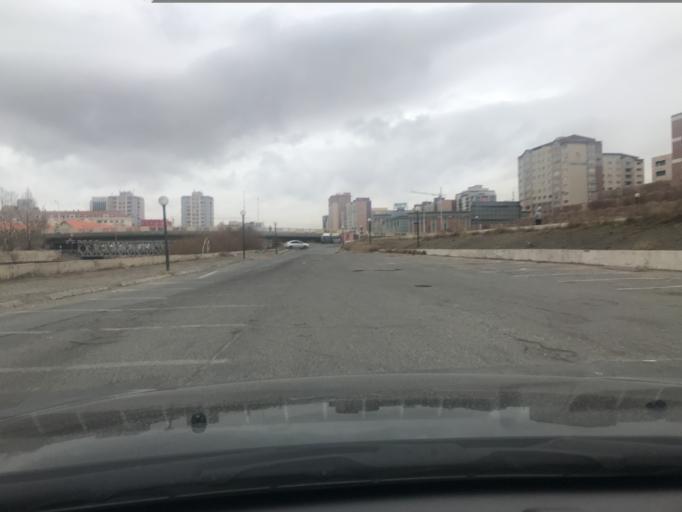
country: MN
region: Ulaanbaatar
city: Ulaanbaatar
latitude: 47.9219
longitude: 106.9321
